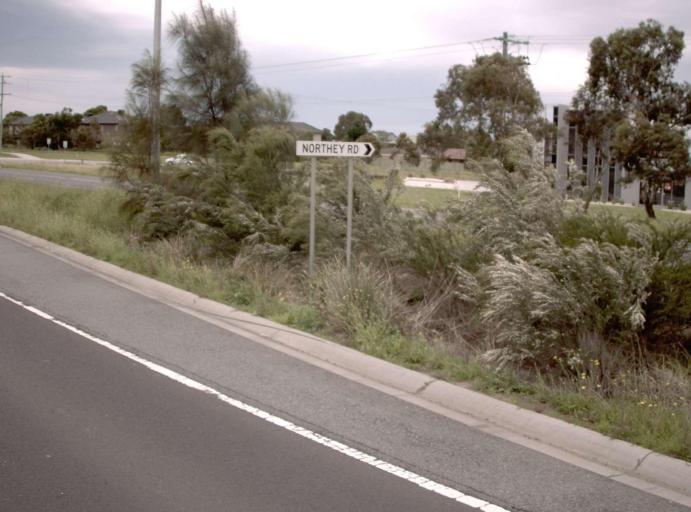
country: AU
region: Victoria
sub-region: Casey
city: Lynbrook
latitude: -38.0452
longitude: 145.2541
